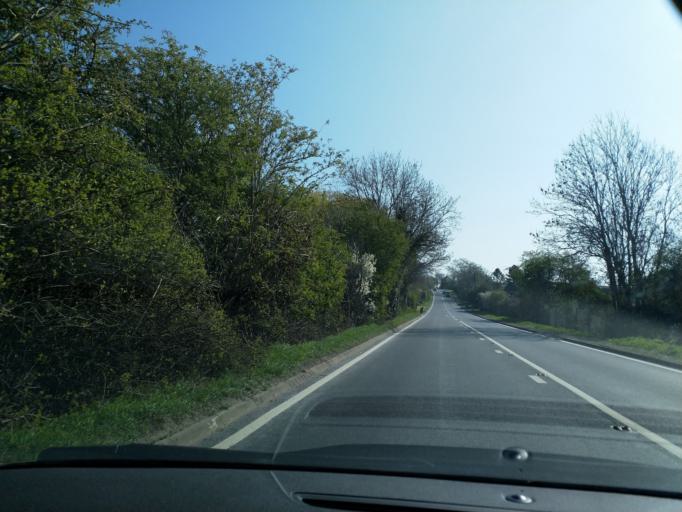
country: GB
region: England
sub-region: Warwickshire
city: Stratford-upon-Avon
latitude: 52.1836
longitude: -1.7550
